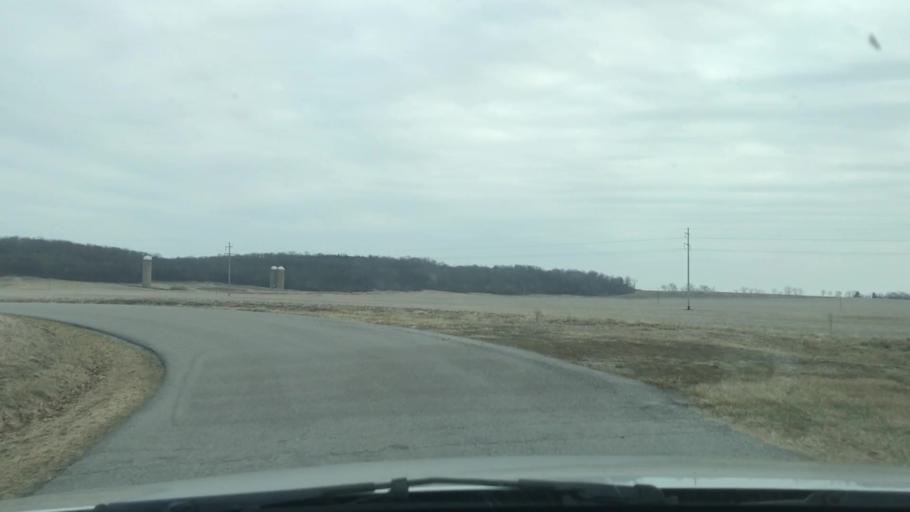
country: US
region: Kentucky
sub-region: Edmonson County
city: Brownsville
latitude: 37.0491
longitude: -86.2412
